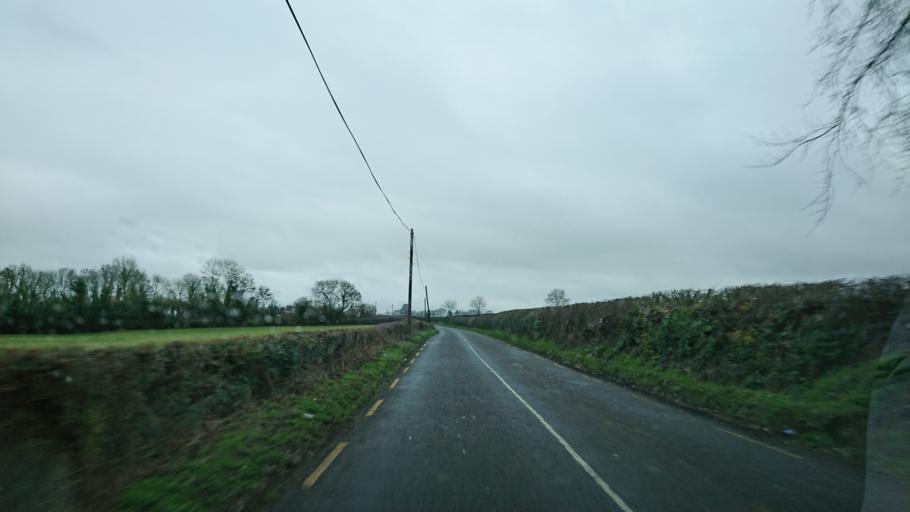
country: IE
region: Leinster
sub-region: Kilkenny
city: Callan
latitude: 52.5306
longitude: -7.2972
